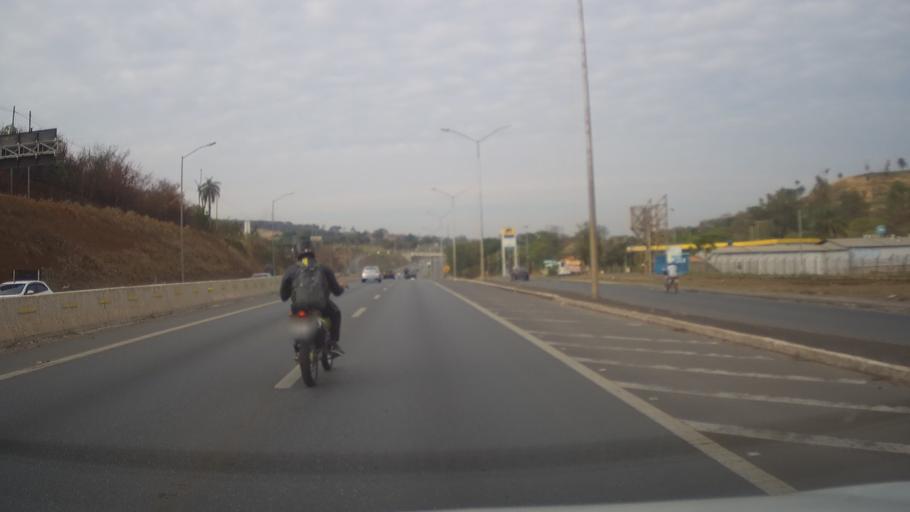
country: BR
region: Minas Gerais
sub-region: Vespasiano
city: Vespasiano
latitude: -19.7167
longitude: -43.9287
